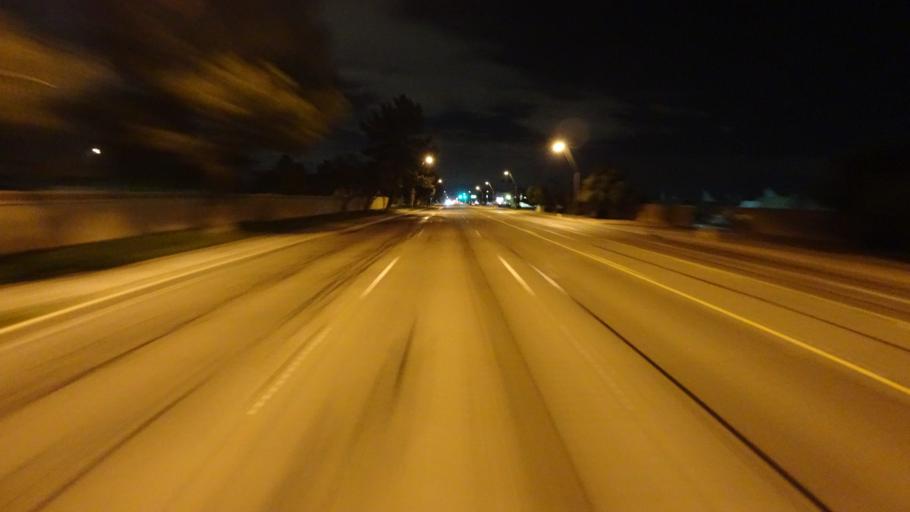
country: US
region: Arizona
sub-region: Maricopa County
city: Guadalupe
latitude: 33.3254
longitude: -111.9284
